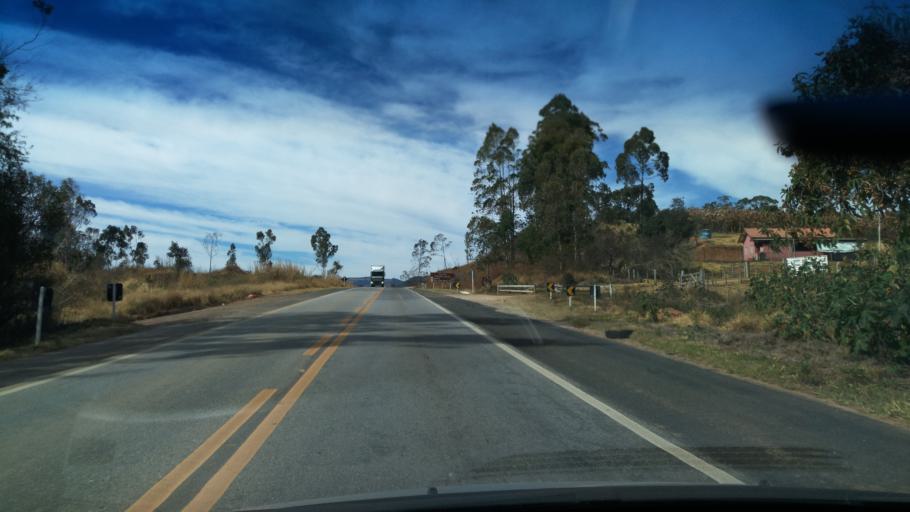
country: BR
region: Minas Gerais
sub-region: Borda Da Mata
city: Borda da Mata
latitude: -22.0597
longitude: -46.2822
